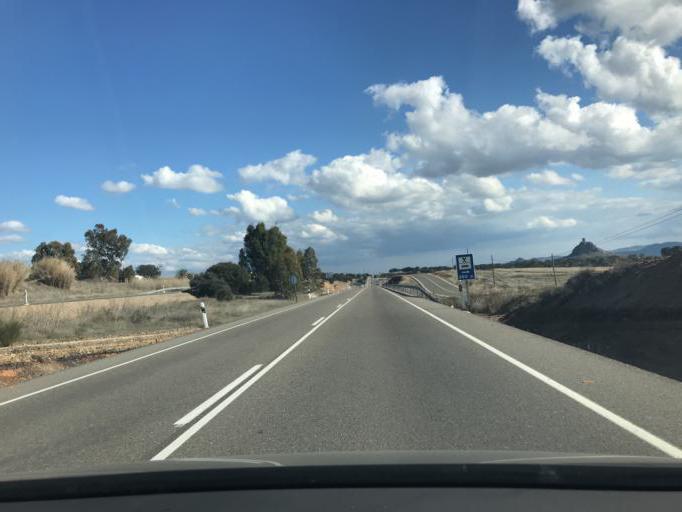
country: ES
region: Andalusia
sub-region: Province of Cordoba
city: Penarroya-Pueblonuevo
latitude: 38.2925
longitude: -5.2308
